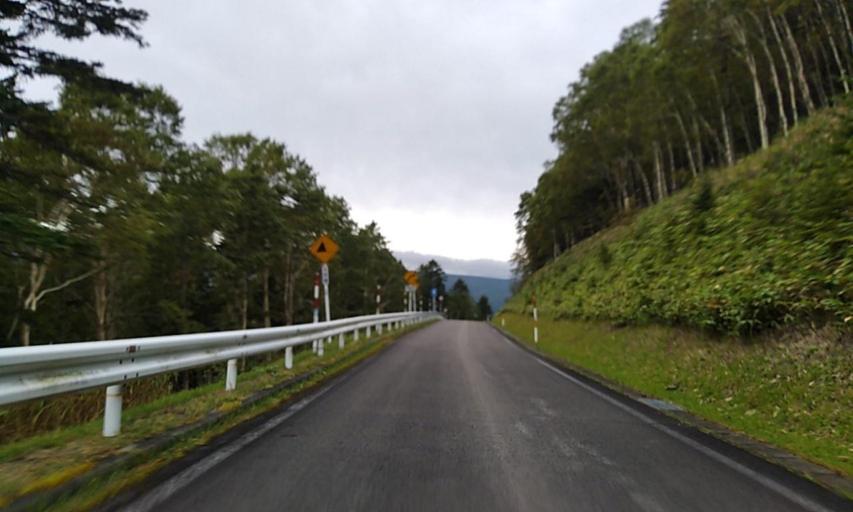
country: JP
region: Hokkaido
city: Bihoro
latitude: 43.5653
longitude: 144.2229
